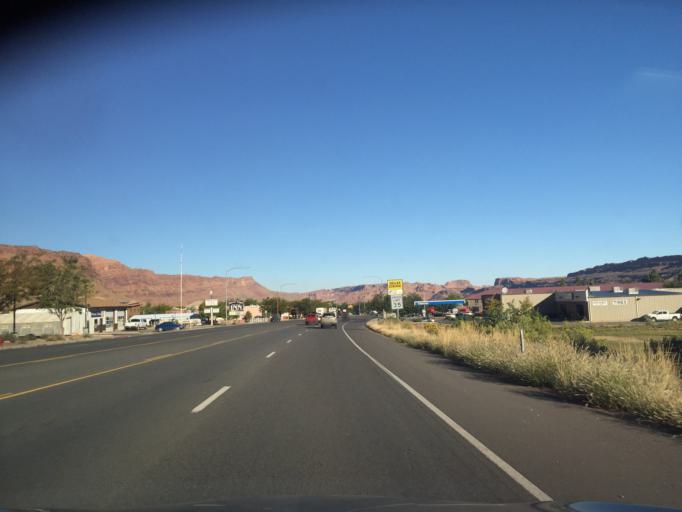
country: US
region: Utah
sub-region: Grand County
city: Moab
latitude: 38.5595
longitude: -109.5458
